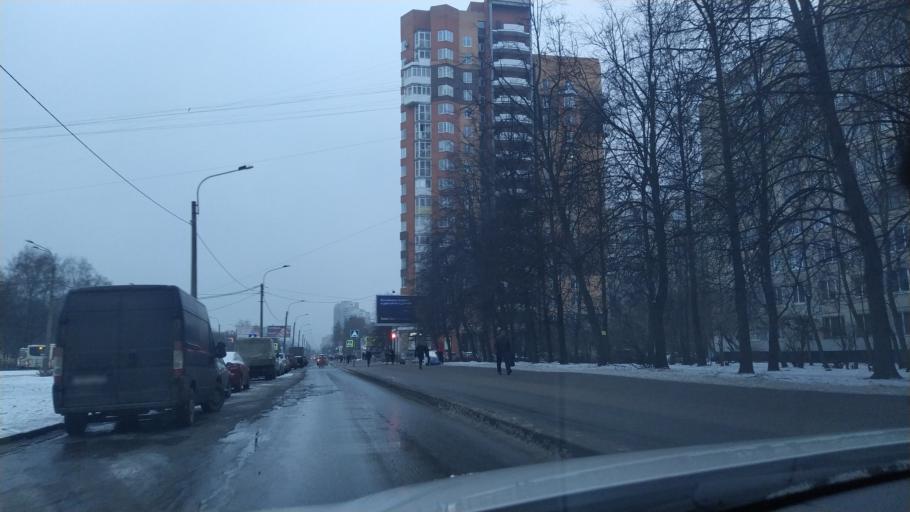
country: RU
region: Leningrad
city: Akademicheskoe
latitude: 60.0180
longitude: 30.4019
